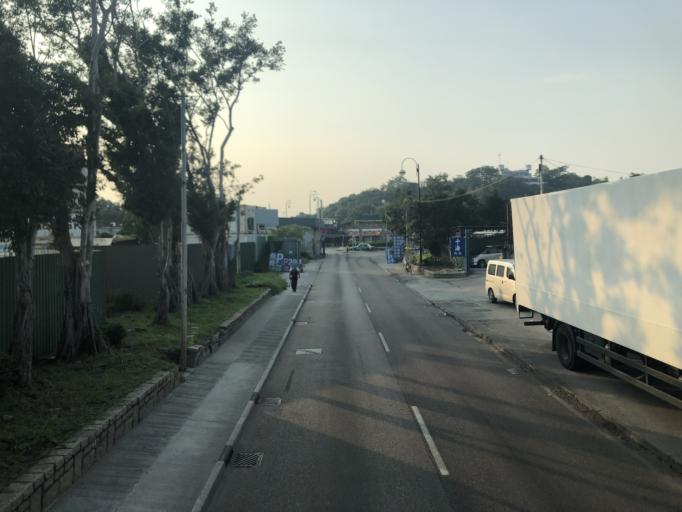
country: HK
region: Yuen Long
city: Yuen Long Kau Hui
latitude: 22.4664
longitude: 113.9848
